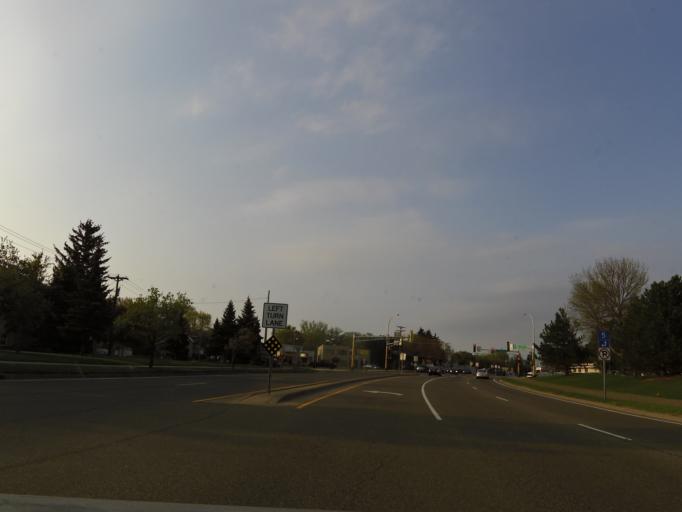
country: US
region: Minnesota
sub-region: Ramsey County
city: Maplewood
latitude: 44.9621
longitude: -93.0049
